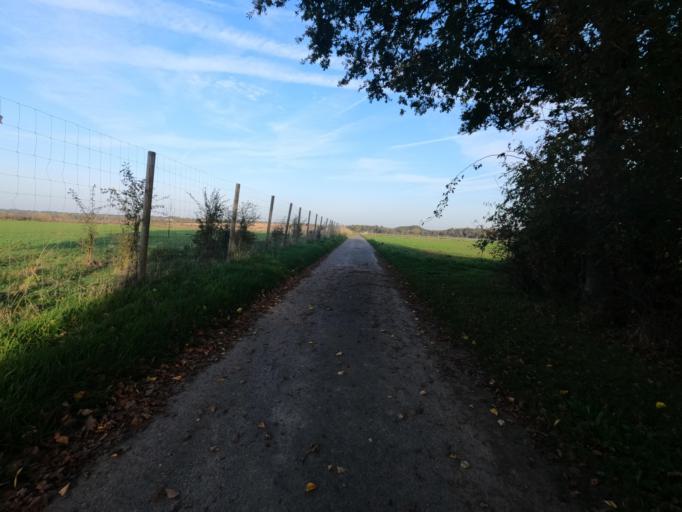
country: DE
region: North Rhine-Westphalia
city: Erkelenz
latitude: 51.0504
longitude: 6.3686
